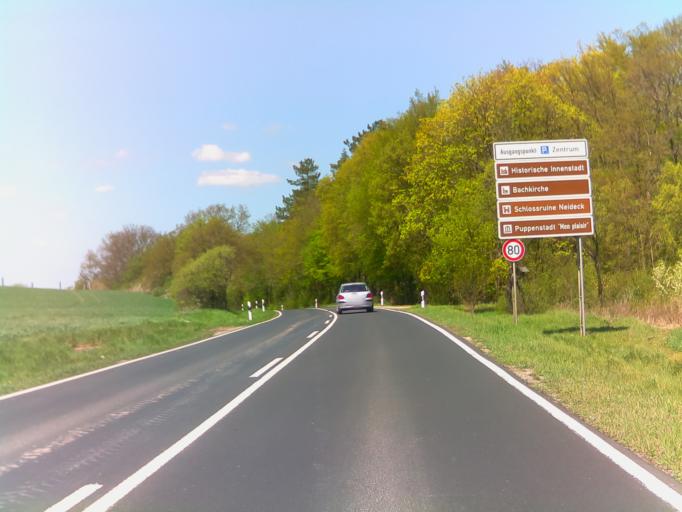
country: DE
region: Thuringia
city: Dornheim
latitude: 50.8116
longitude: 10.9754
